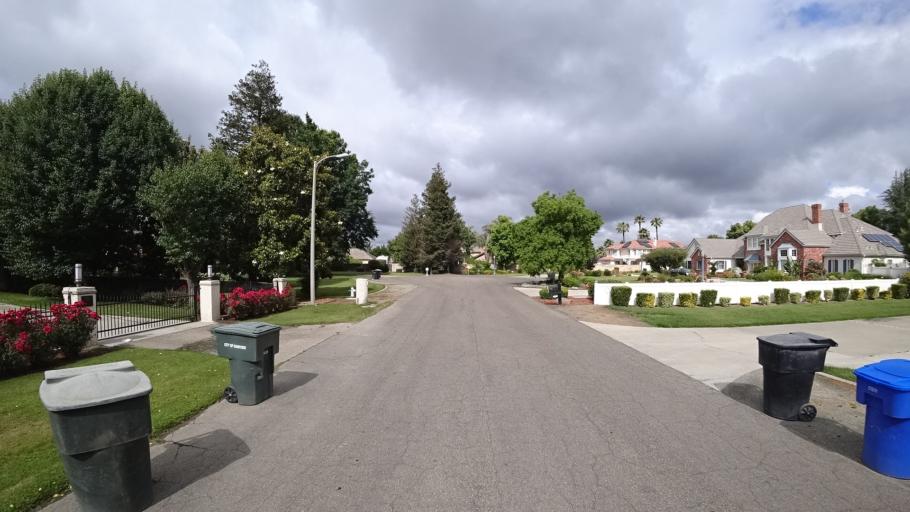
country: US
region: California
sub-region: Kings County
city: Lucerne
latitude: 36.3527
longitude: -119.6741
